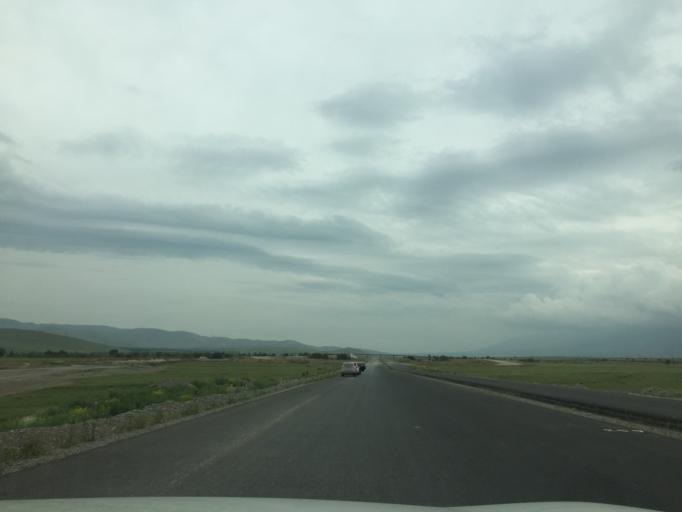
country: KZ
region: Ongtustik Qazaqstan
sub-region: Tulkibas Audany
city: Zhabagly
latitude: 42.5069
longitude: 70.4601
